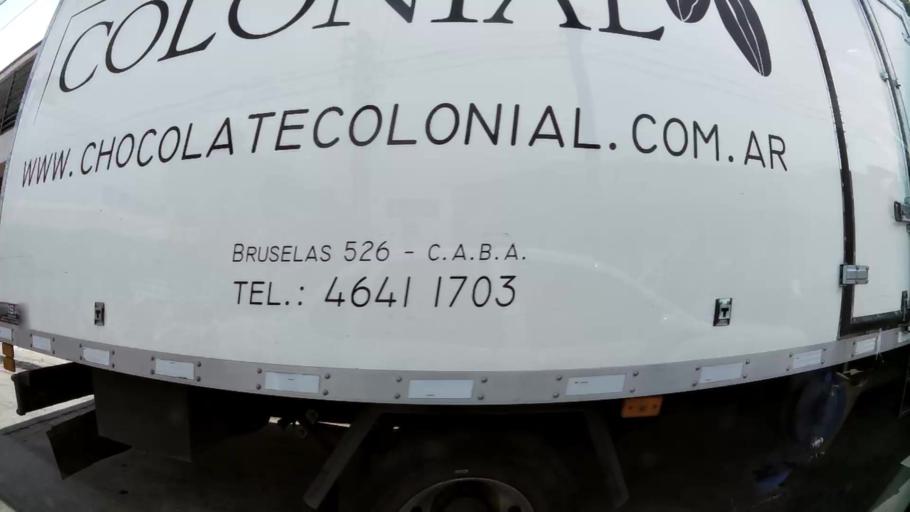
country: AR
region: Buenos Aires
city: San Justo
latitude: -34.6867
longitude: -58.5499
